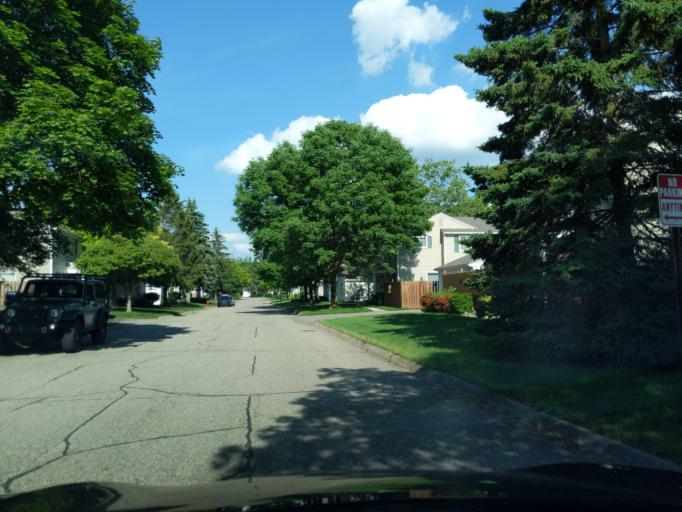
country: US
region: Michigan
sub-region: Ingham County
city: Lansing
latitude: 42.7573
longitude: -84.5257
